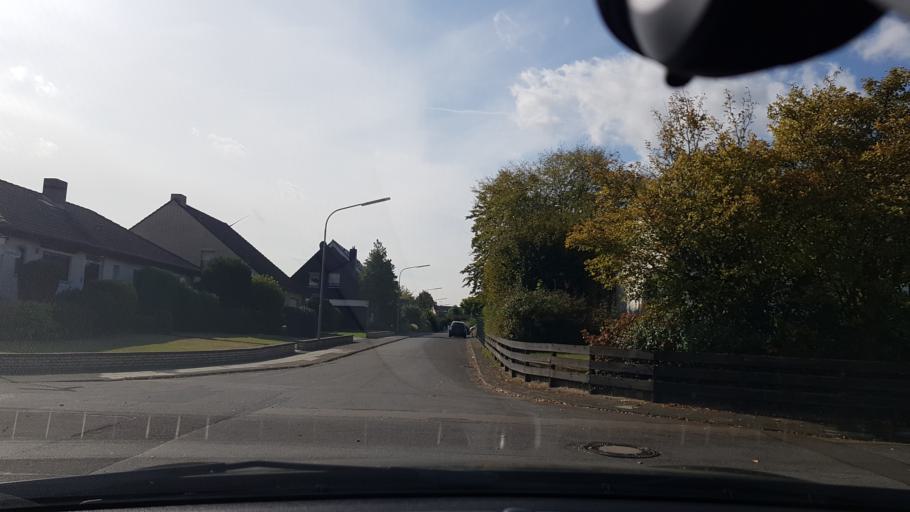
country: DE
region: North Rhine-Westphalia
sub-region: Regierungsbezirk Dusseldorf
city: Neuss
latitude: 51.1425
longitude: 6.6996
